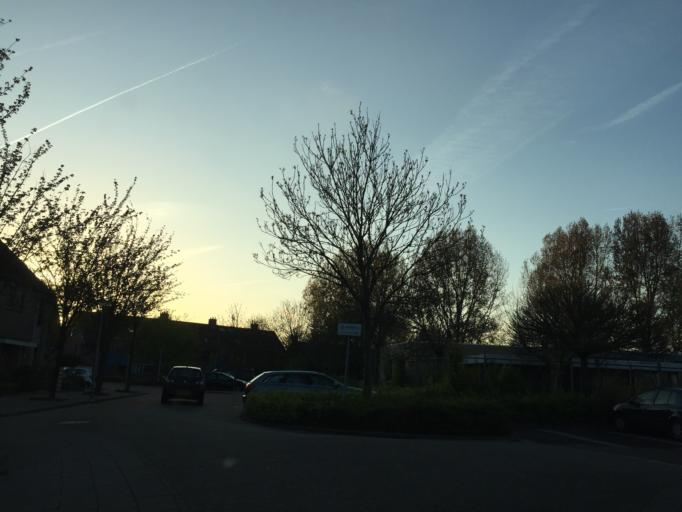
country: NL
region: South Holland
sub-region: Gemeente Voorschoten
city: Voorschoten
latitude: 52.1412
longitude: 4.4594
